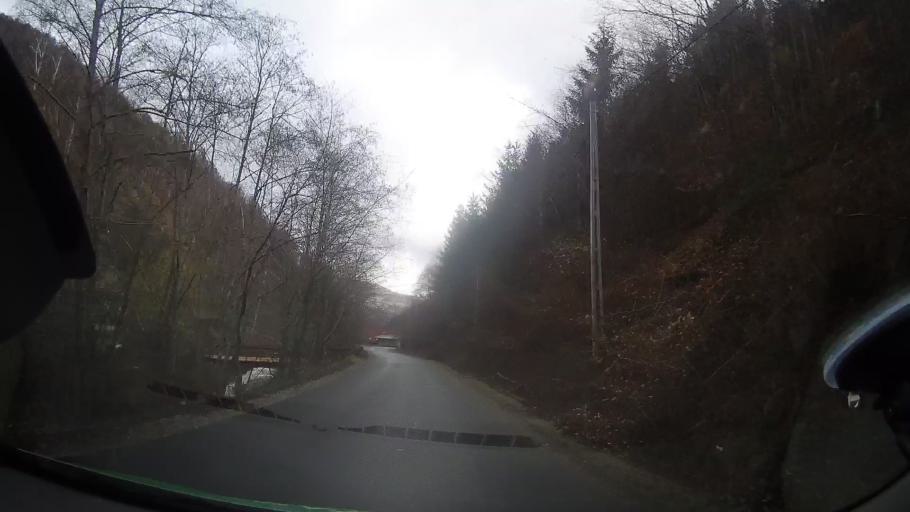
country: RO
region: Cluj
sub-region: Comuna Valea Ierii
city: Valea Ierii
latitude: 46.6427
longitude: 23.3214
